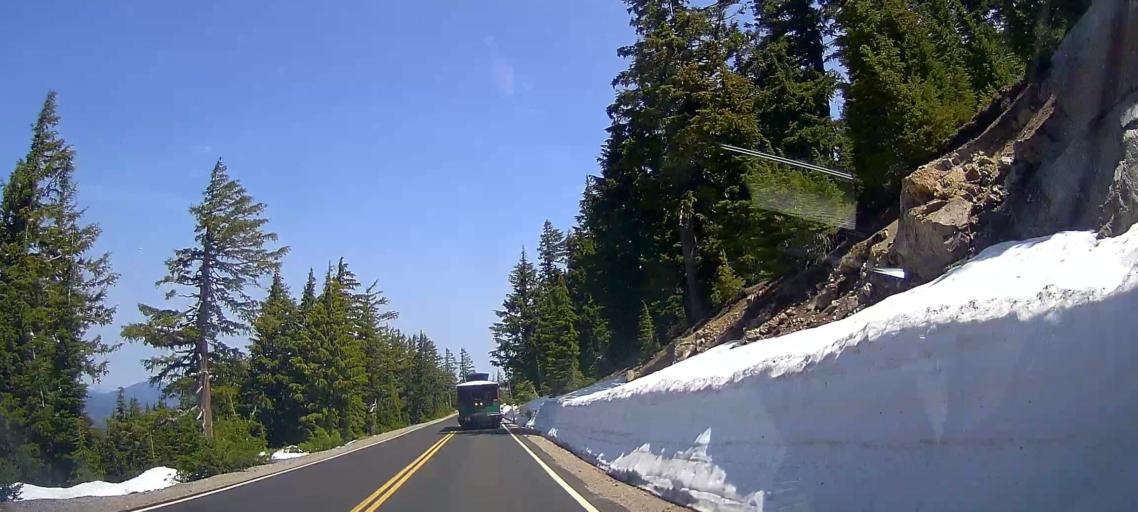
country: US
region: Oregon
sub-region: Jackson County
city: Shady Cove
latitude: 42.9757
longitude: -122.1433
